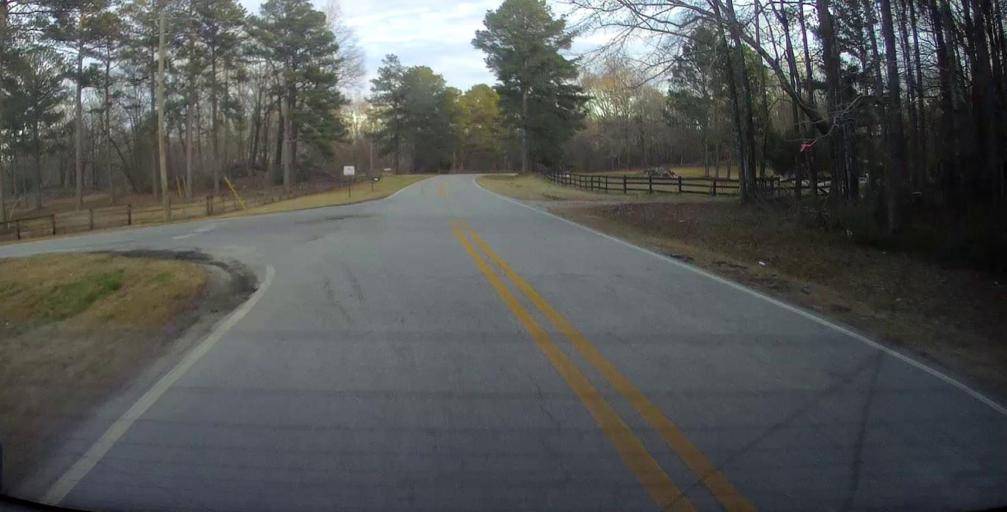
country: US
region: Georgia
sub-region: Harris County
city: Hamilton
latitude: 32.5995
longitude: -84.8782
